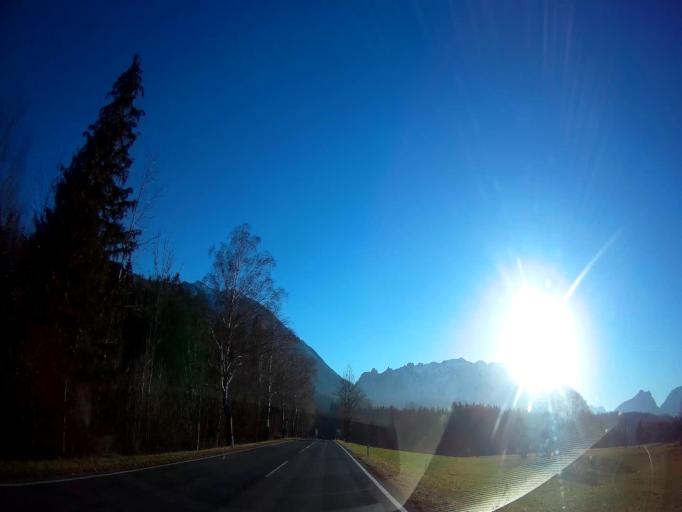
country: DE
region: Bavaria
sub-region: Upper Bavaria
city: Piding
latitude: 47.7551
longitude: 12.9444
